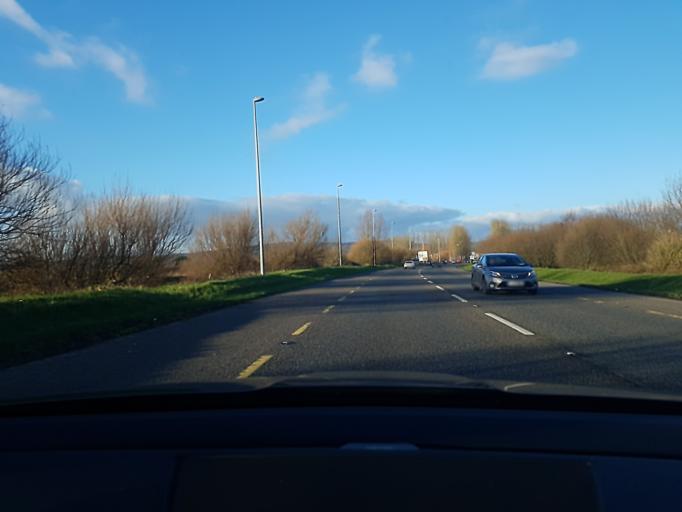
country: IE
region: Munster
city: Moyross
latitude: 52.6704
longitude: -8.6749
